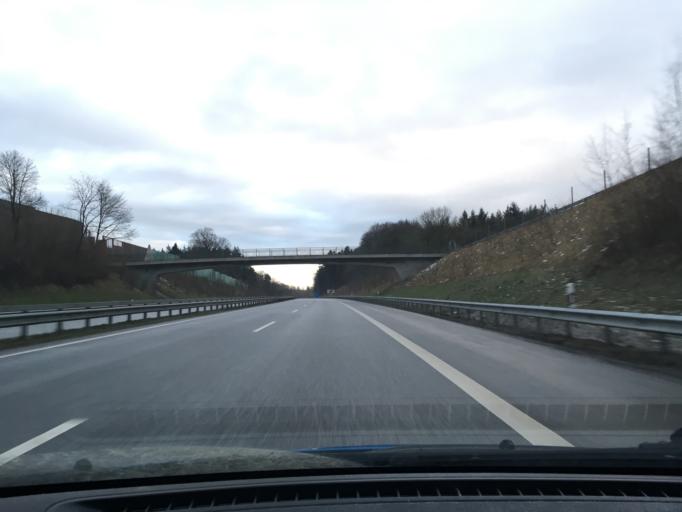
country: DE
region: Schleswig-Holstein
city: Heiligenstedten
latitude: 53.9496
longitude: 9.4876
